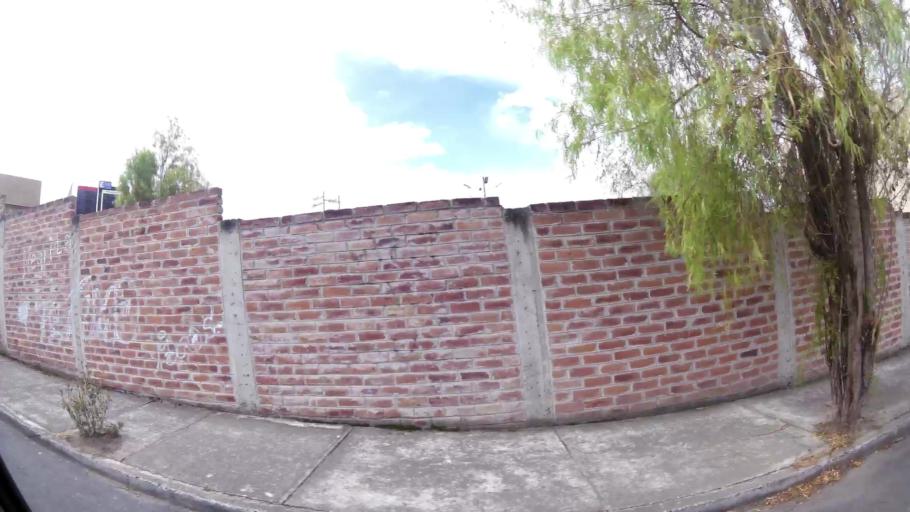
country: EC
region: Tungurahua
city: Ambato
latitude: -1.2748
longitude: -78.6392
